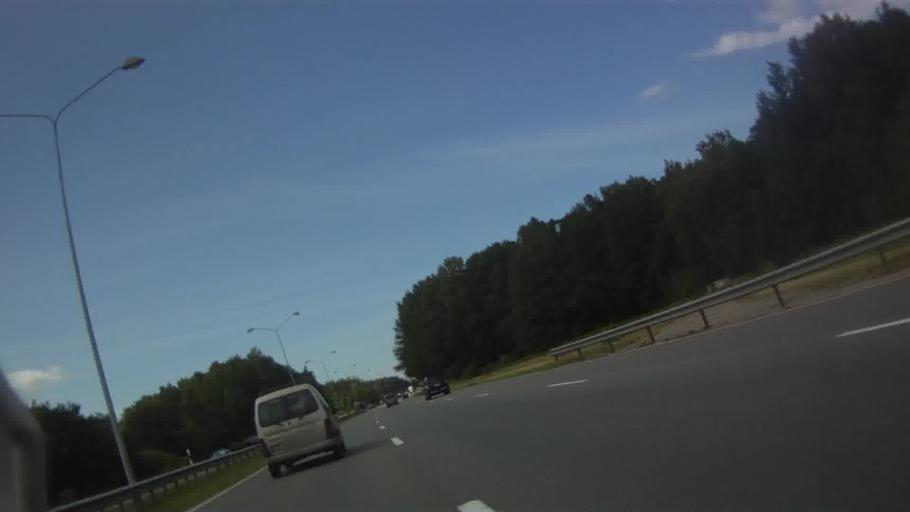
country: LV
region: Babite
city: Pinki
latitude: 56.9636
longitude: 23.8787
